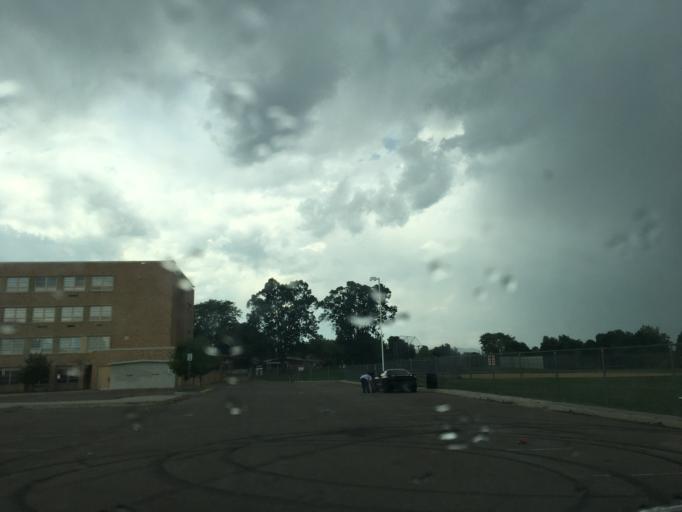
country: US
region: Colorado
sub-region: Arapahoe County
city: Sheridan
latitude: 39.6766
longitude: -105.0391
